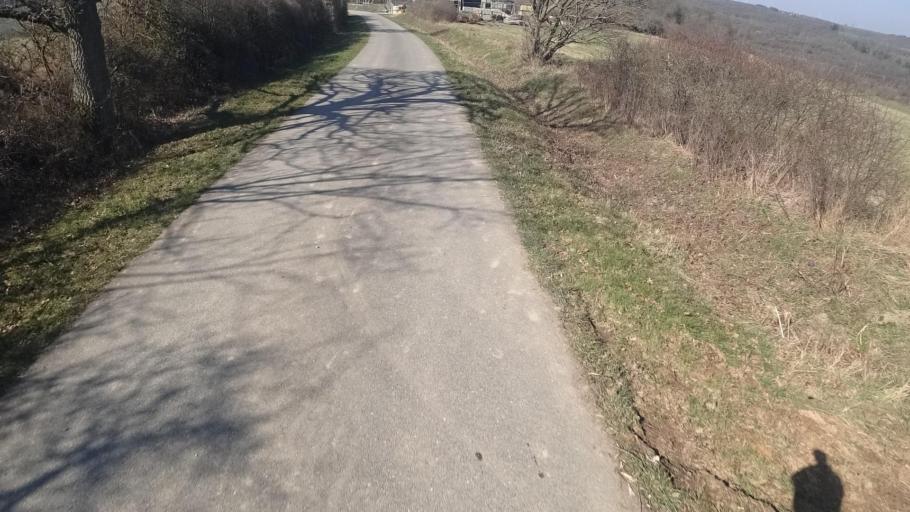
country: DE
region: Rheinland-Pfalz
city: Gemunden
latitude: 49.9004
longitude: 7.4804
